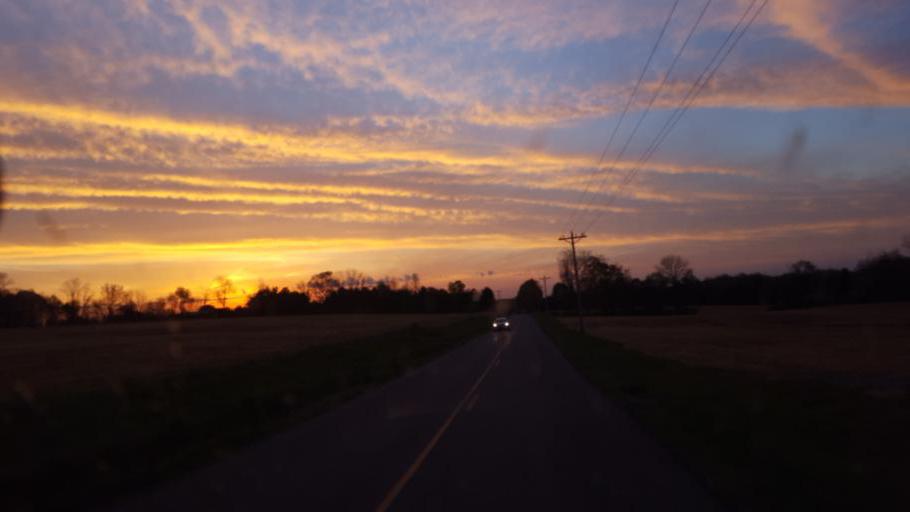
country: US
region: Ohio
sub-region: Knox County
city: Mount Vernon
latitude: 40.4726
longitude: -82.4348
